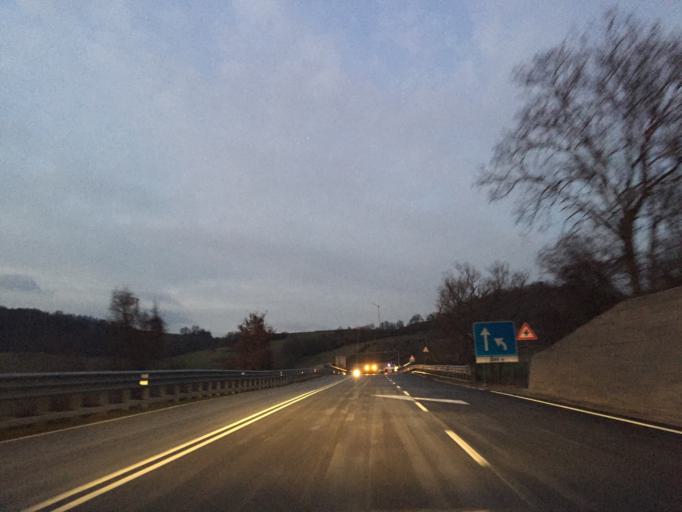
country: IT
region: Apulia
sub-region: Provincia di Foggia
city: Volturino
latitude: 41.4655
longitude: 15.0938
